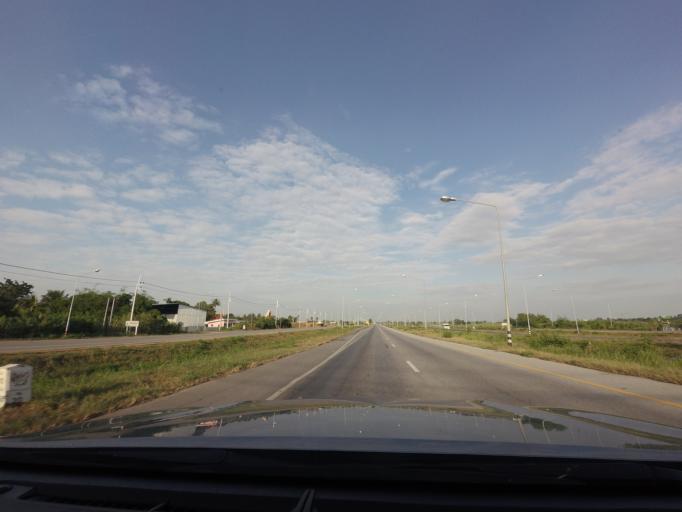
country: TH
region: Nakhon Sawan
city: Nakhon Sawan
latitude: 15.7559
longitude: 100.0898
